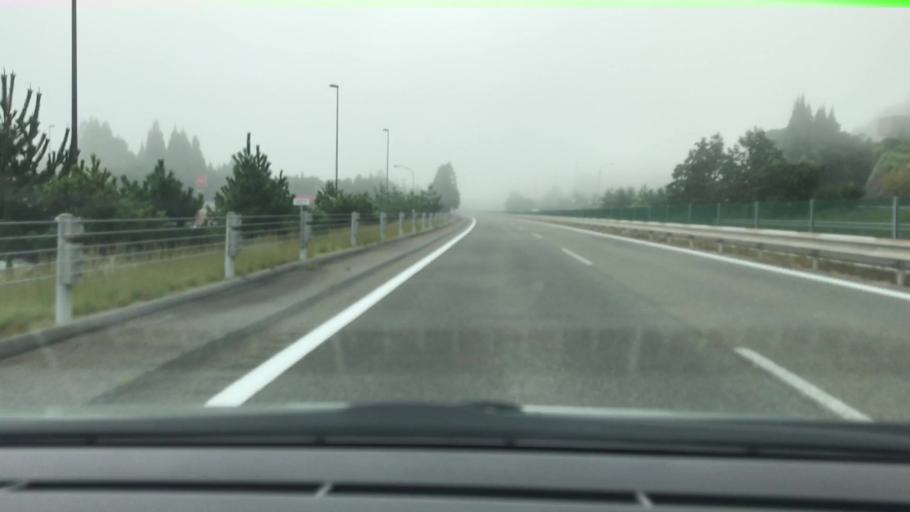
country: JP
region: Hyogo
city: Sasayama
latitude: 35.0929
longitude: 135.1679
